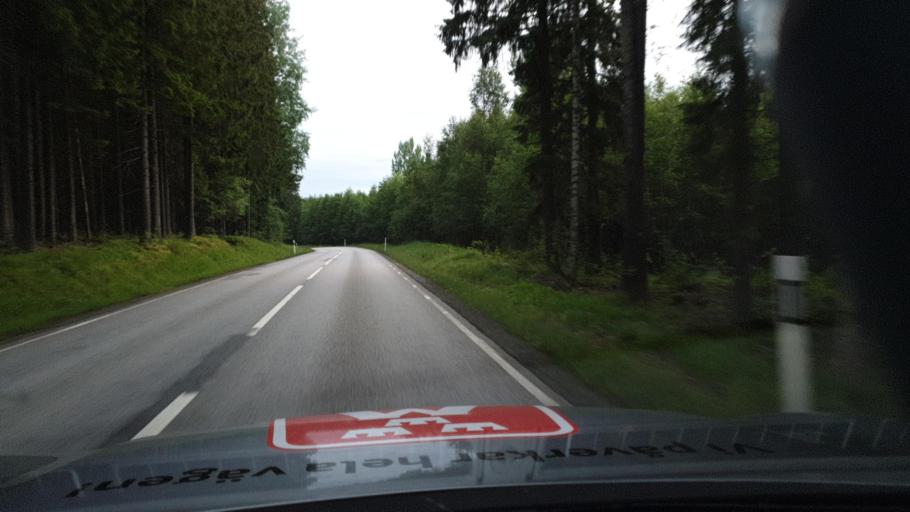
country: SE
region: OErebro
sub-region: Ljusnarsbergs Kommun
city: Kopparberg
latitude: 59.8658
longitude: 15.0026
